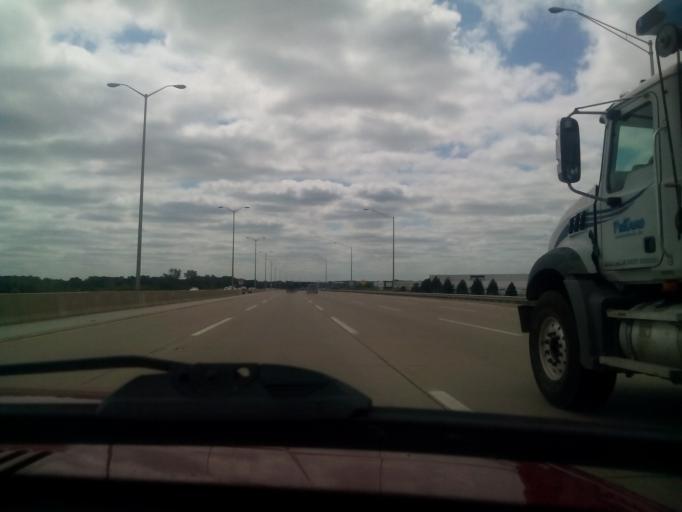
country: US
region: Illinois
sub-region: Cook County
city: Lemont
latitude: 41.6937
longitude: -88.0301
